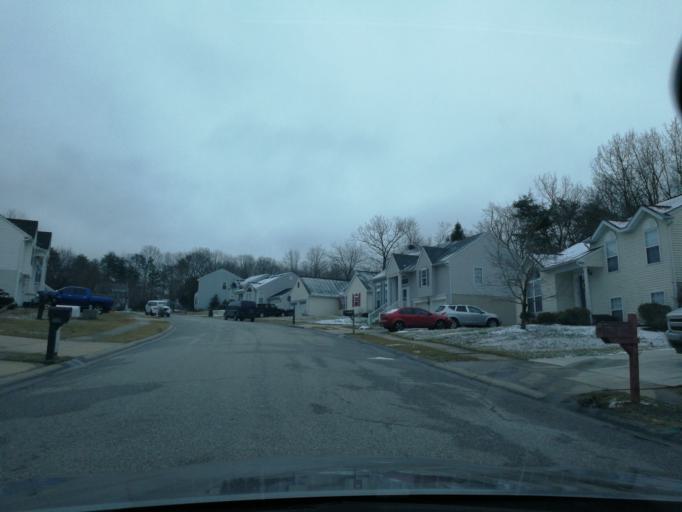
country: US
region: Maryland
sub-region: Harford County
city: Bel Air South
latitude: 39.4685
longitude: -76.2966
